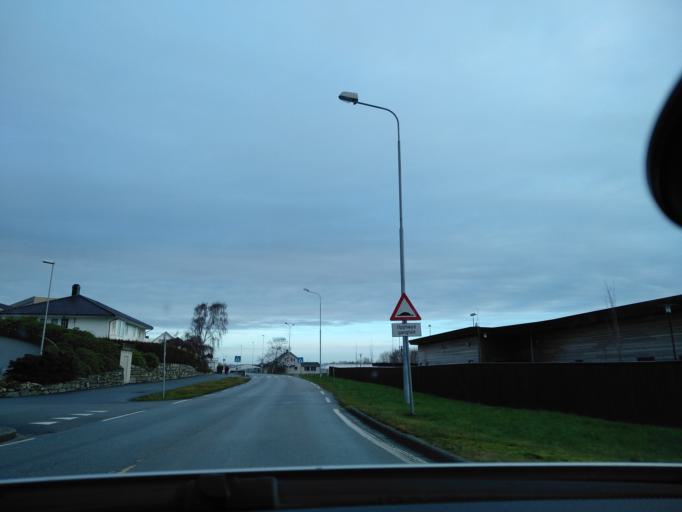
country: NO
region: Rogaland
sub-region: Randaberg
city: Randaberg
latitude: 59.0010
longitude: 5.6264
